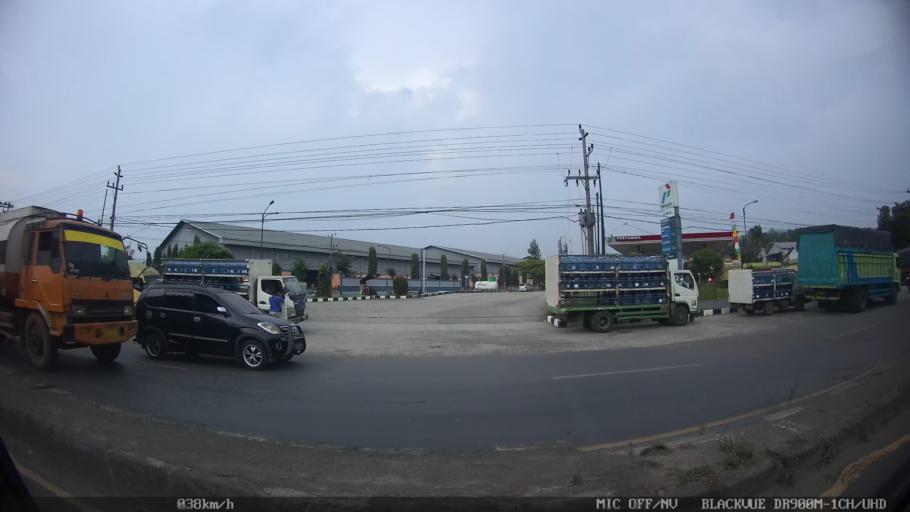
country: ID
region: Lampung
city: Bandarlampung
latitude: -5.4088
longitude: 105.2952
